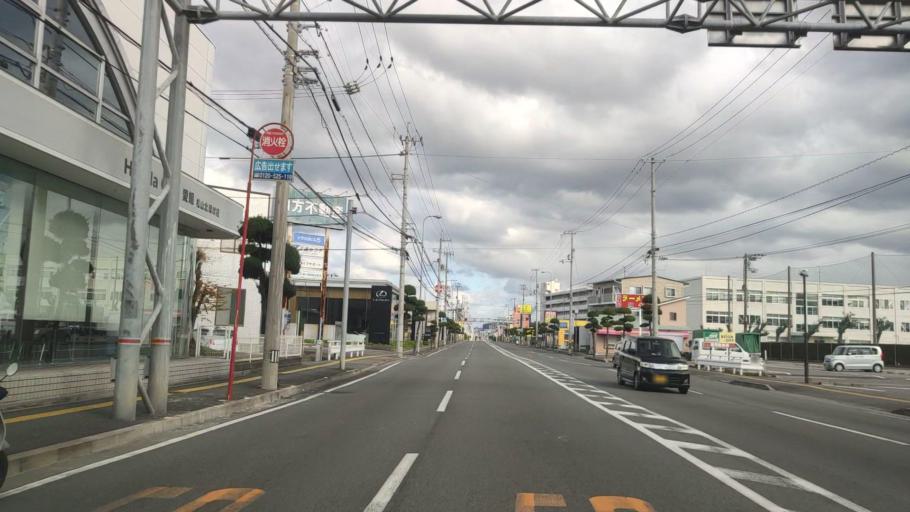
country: JP
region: Ehime
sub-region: Shikoku-chuo Shi
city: Matsuyama
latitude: 33.8557
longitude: 132.7481
